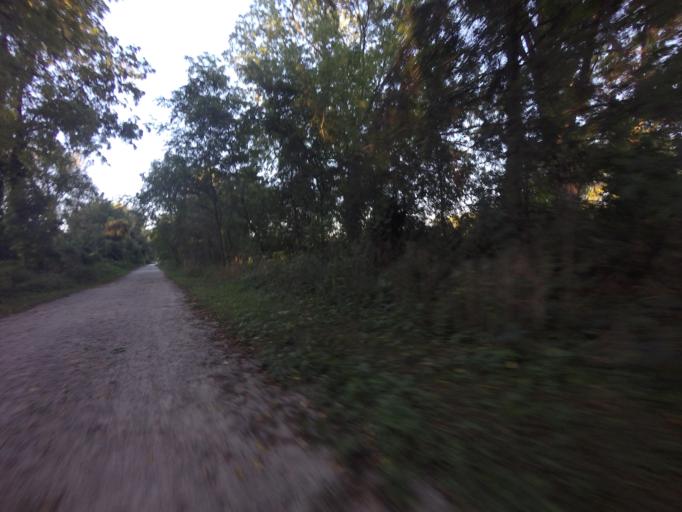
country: CA
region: Ontario
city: Brampton
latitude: 43.8762
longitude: -79.8556
